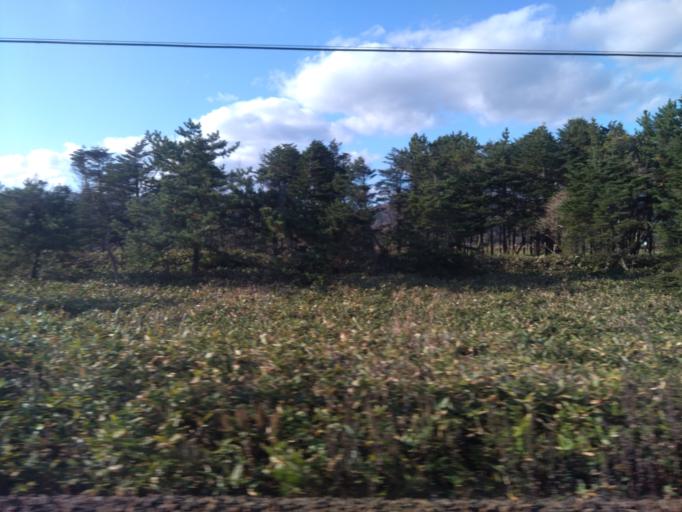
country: JP
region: Hokkaido
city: Niseko Town
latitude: 42.5774
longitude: 140.4512
